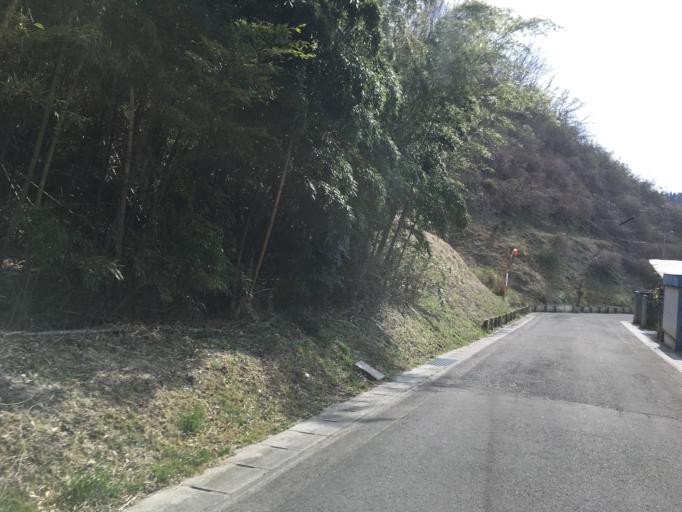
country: JP
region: Fukushima
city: Hobaramachi
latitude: 37.6592
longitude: 140.6108
